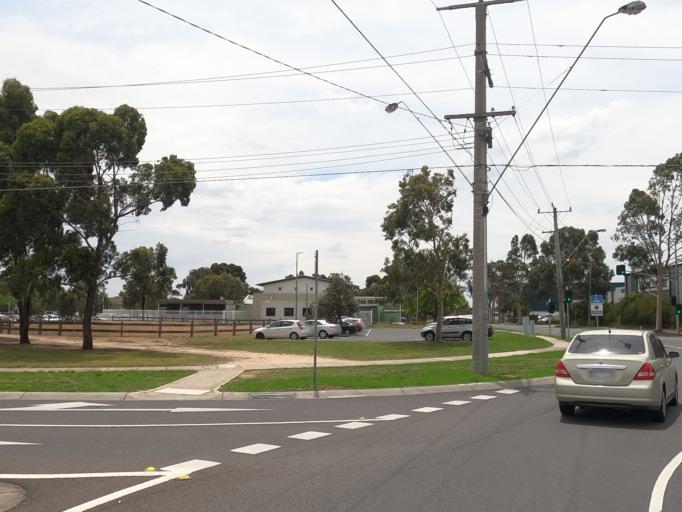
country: AU
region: Victoria
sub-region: Hume
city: Broadmeadows
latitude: -37.6775
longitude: 144.9192
